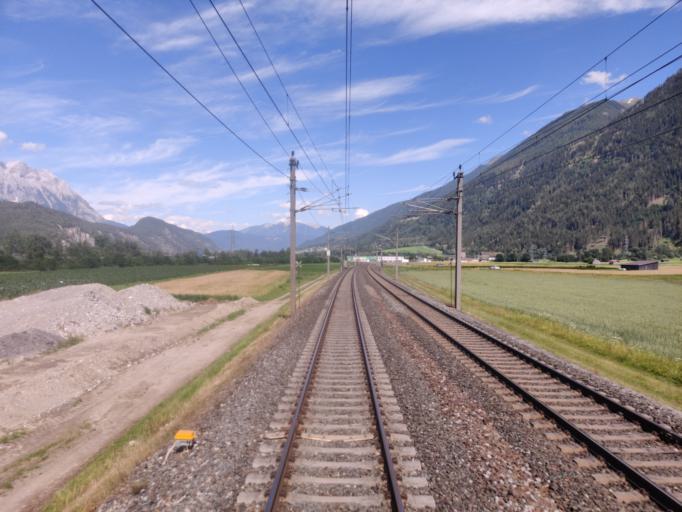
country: AT
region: Tyrol
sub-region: Politischer Bezirk Imst
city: Silz
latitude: 47.2712
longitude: 10.9436
